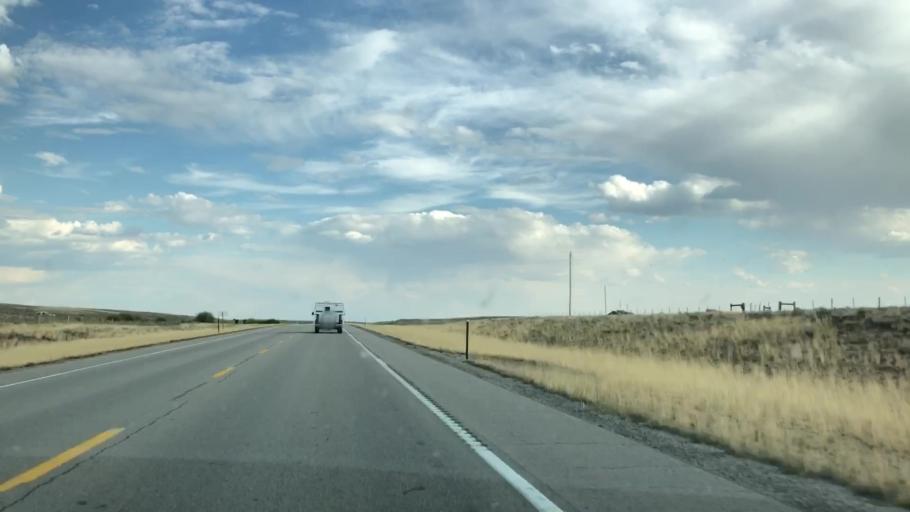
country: US
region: Wyoming
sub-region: Sublette County
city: Pinedale
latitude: 43.0168
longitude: -110.1165
